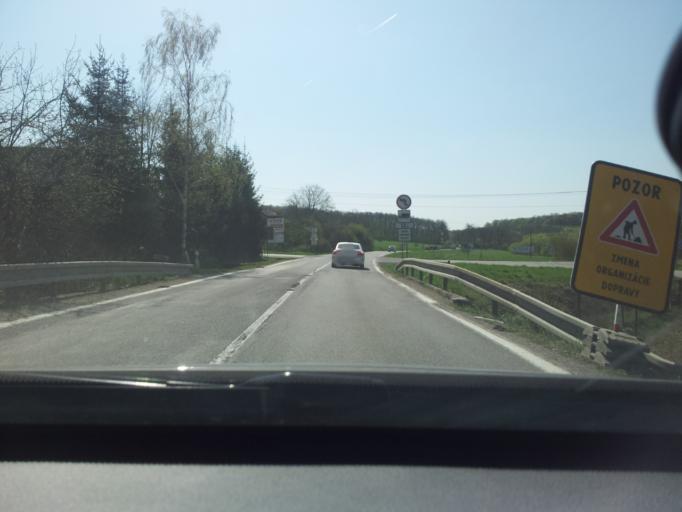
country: SK
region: Nitriansky
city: Banovce nad Bebravou
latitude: 48.7804
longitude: 18.1782
